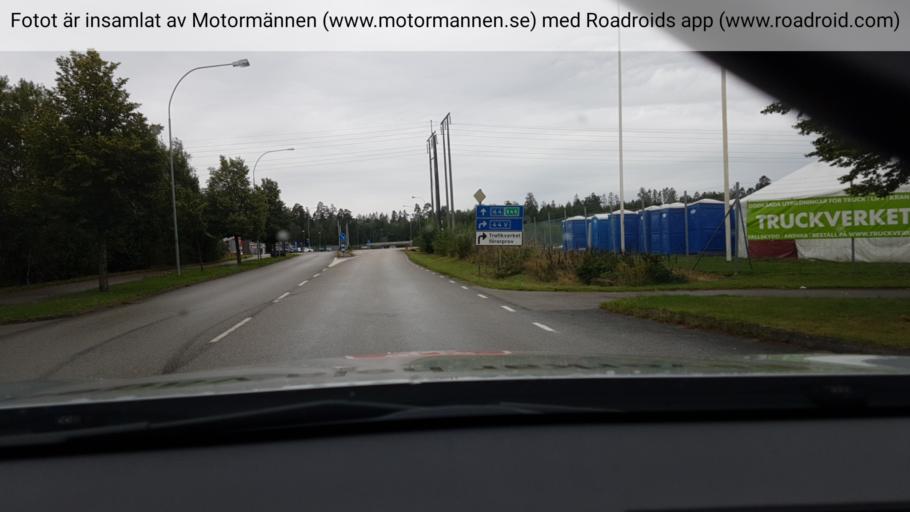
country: SE
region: Vaestra Goetaland
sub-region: Trollhattan
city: Trollhattan
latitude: 58.3416
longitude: 12.2539
